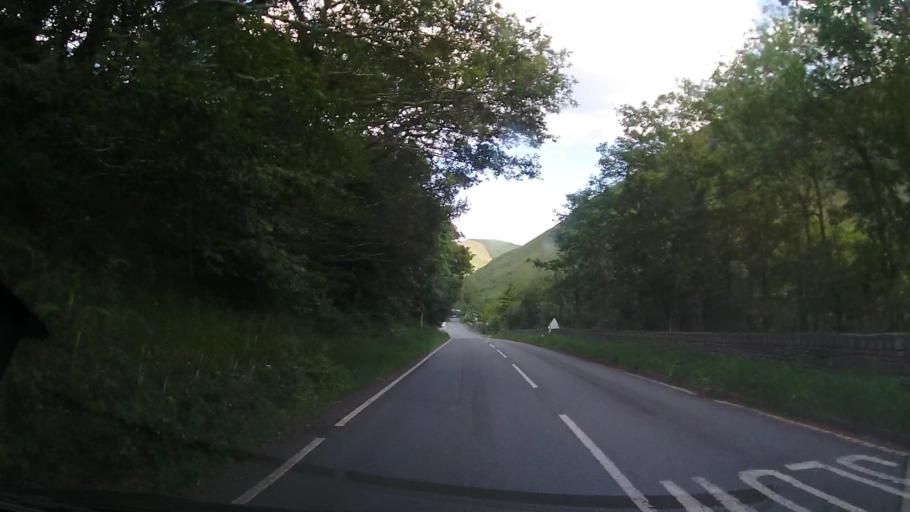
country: GB
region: Wales
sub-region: Gwynedd
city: Corris
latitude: 52.6666
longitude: -3.9099
